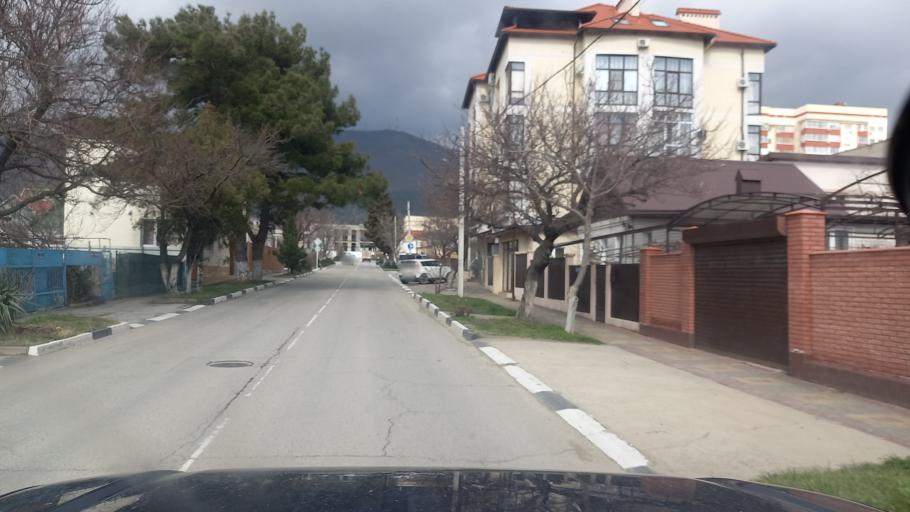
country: RU
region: Krasnodarskiy
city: Gelendzhik
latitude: 44.5595
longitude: 38.0915
